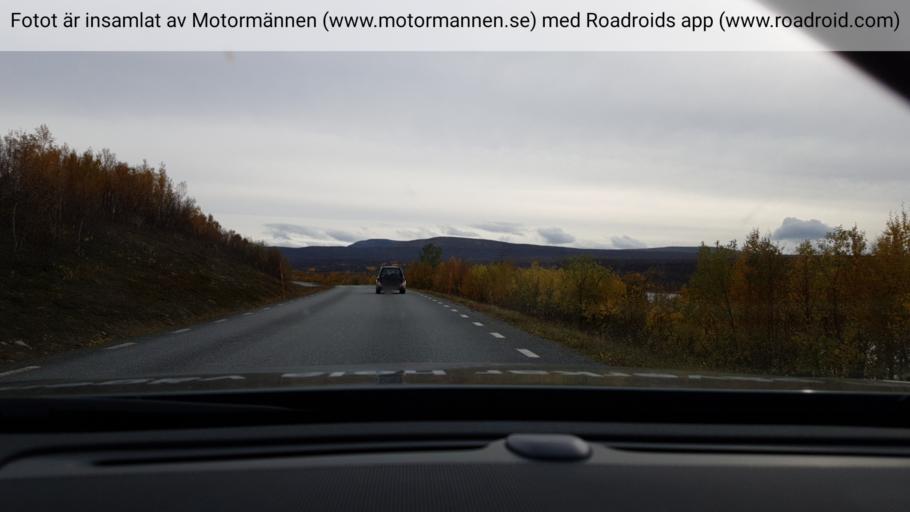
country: NO
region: Nordland
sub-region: Sorfold
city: Straumen
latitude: 66.5048
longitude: 16.4004
